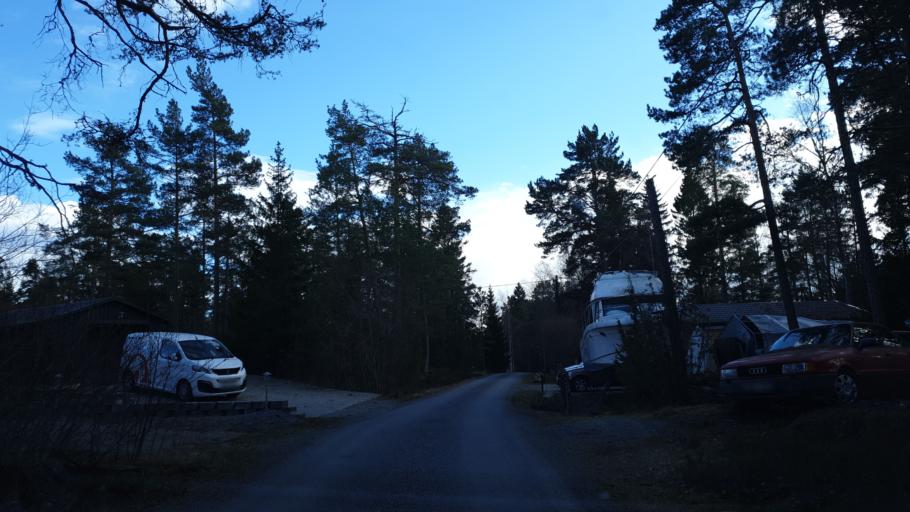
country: SE
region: Stockholm
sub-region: Varmdo Kommun
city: Holo
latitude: 59.2791
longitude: 18.6354
